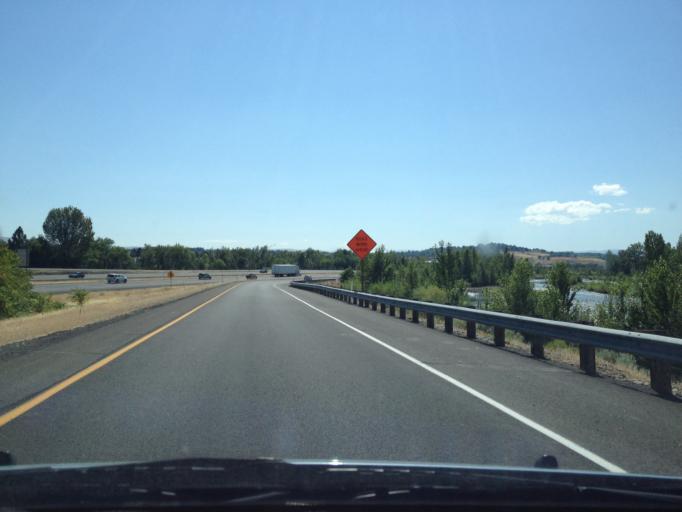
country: US
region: Washington
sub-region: Yakima County
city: Selah
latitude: 46.6245
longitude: -120.5327
